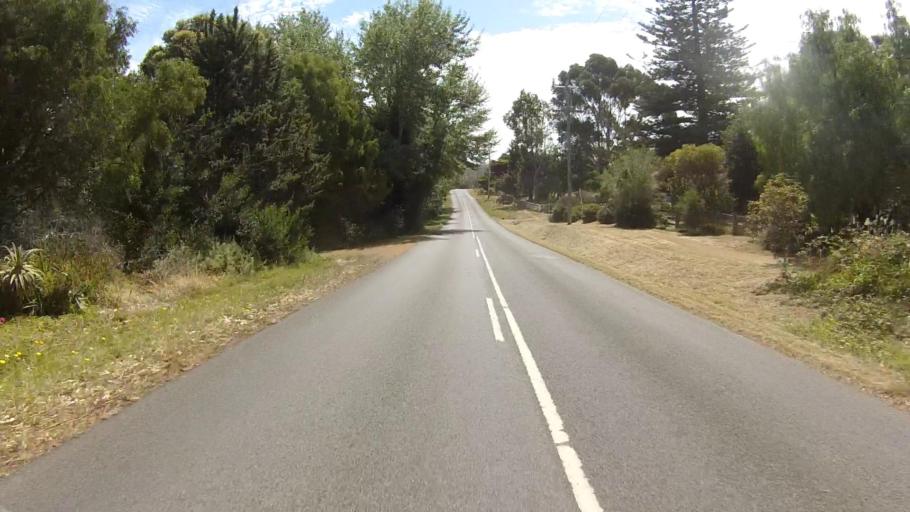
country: AU
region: Tasmania
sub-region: Kingborough
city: Taroona
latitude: -43.0148
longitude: 147.4152
